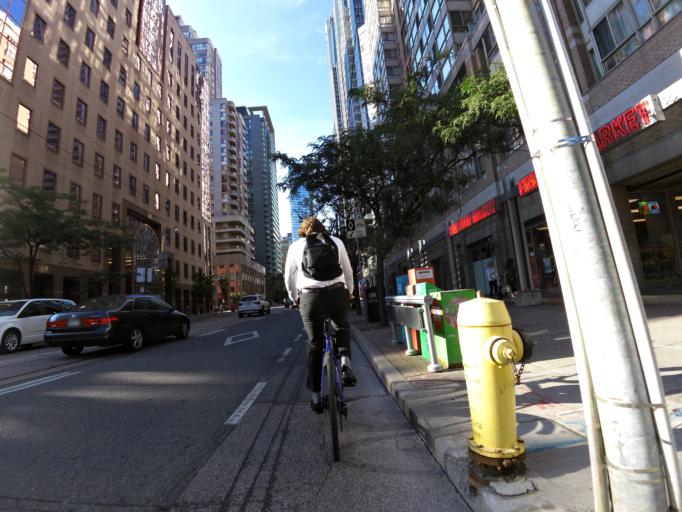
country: CA
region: Ontario
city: Toronto
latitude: 43.6590
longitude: -79.3846
